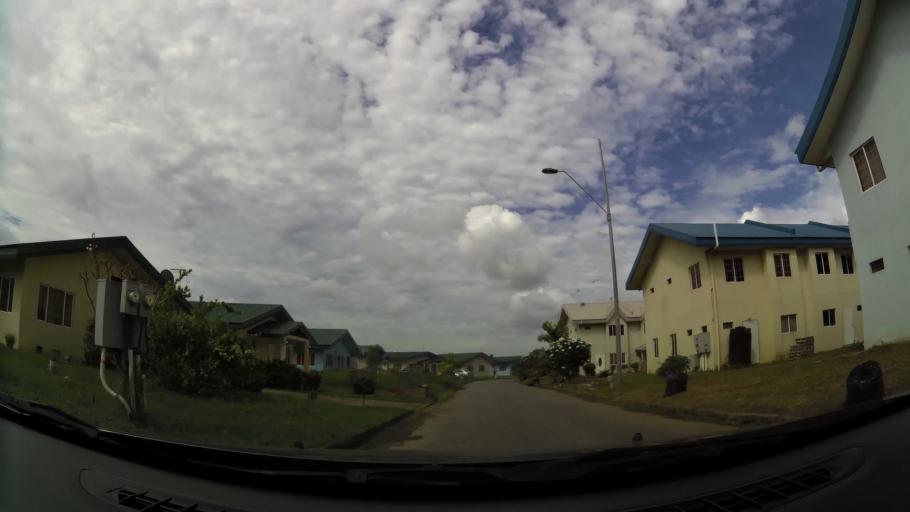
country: TT
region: Chaguanas
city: Chaguanas
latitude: 10.5030
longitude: -61.3988
